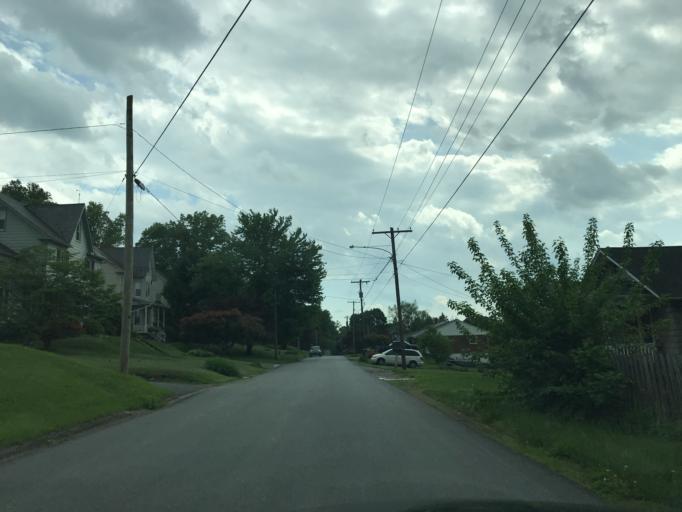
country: US
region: Pennsylvania
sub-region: York County
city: Susquehanna Trails
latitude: 39.7241
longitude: -76.3299
